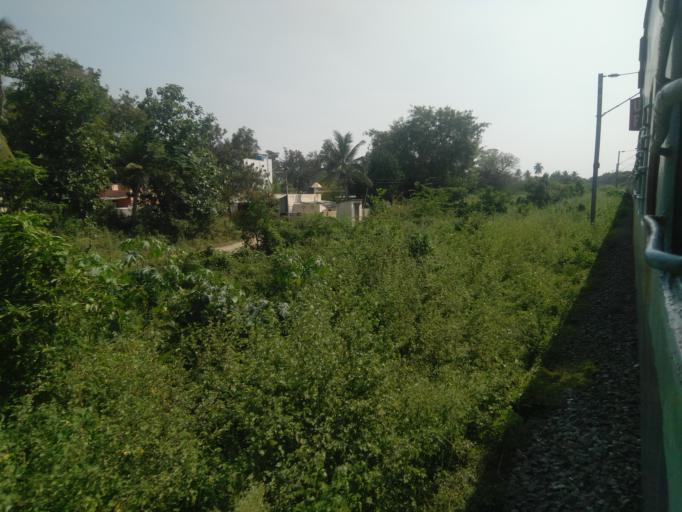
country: IN
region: Tamil Nadu
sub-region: Coimbatore
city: Periyanayakkanpalaiyam
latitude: 11.0965
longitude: 76.9477
